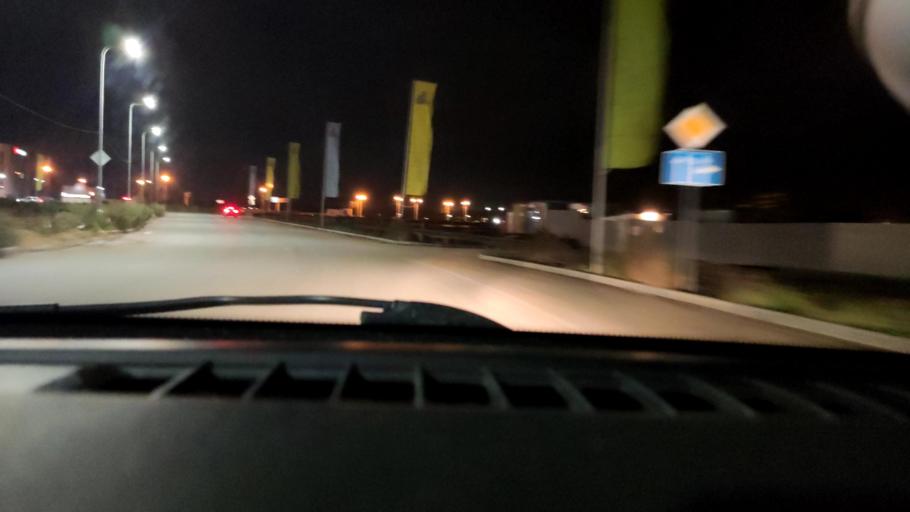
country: RU
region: Samara
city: Samara
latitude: 53.1358
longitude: 50.1702
